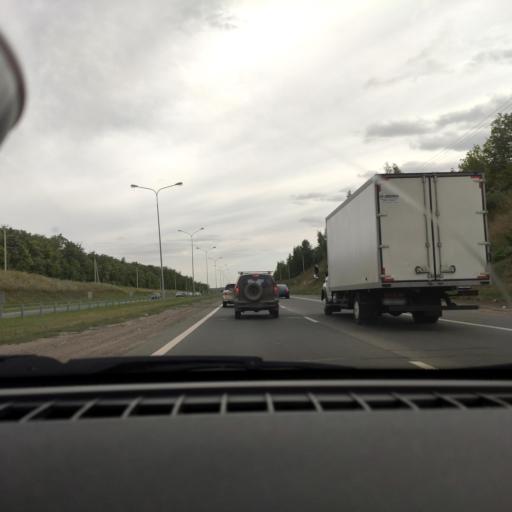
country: RU
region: Samara
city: Novosemeykino
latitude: 53.3663
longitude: 50.3089
